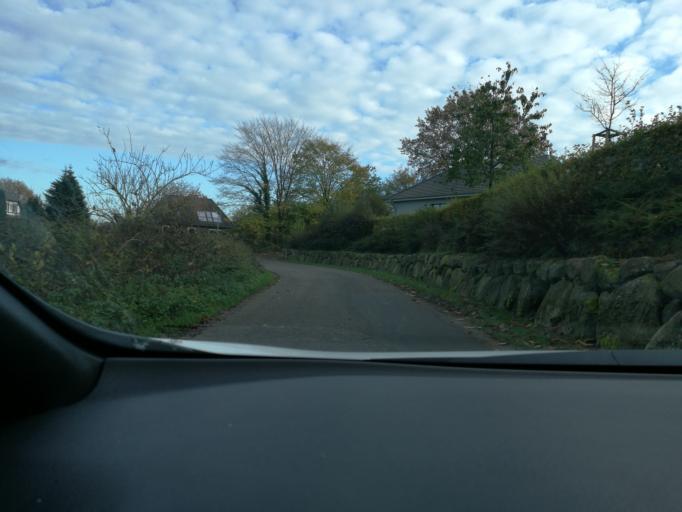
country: DE
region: Schleswig-Holstein
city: Holzbunge
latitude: 54.3829
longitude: 9.7006
